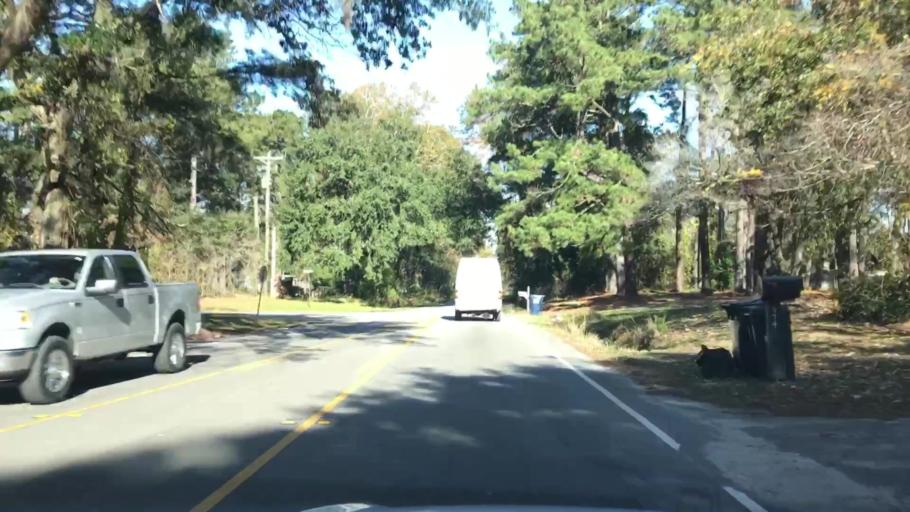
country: US
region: South Carolina
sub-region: Dorchester County
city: Summerville
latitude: 33.0152
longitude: -80.2390
